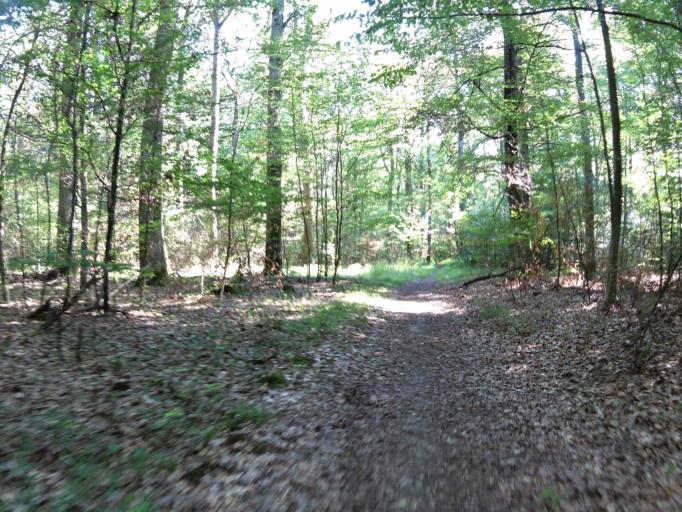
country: DE
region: Bavaria
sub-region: Regierungsbezirk Unterfranken
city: Margetshochheim
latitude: 49.8562
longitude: 9.8768
